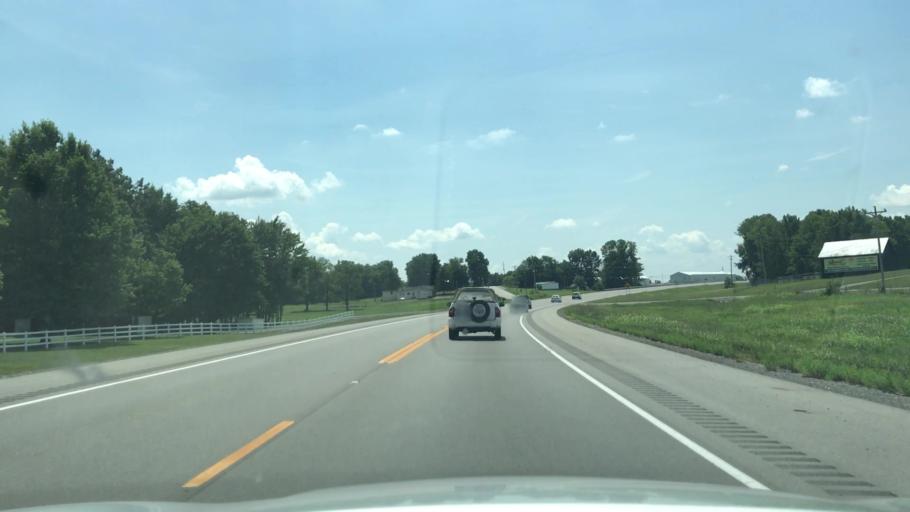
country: US
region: Tennessee
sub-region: Pickett County
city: Byrdstown
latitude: 36.6265
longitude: -85.0899
